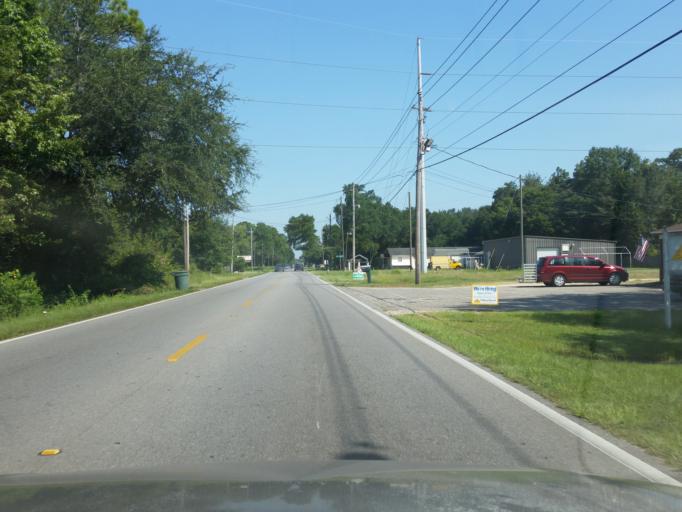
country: US
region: Florida
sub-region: Escambia County
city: Ensley
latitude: 30.5370
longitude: -87.2757
